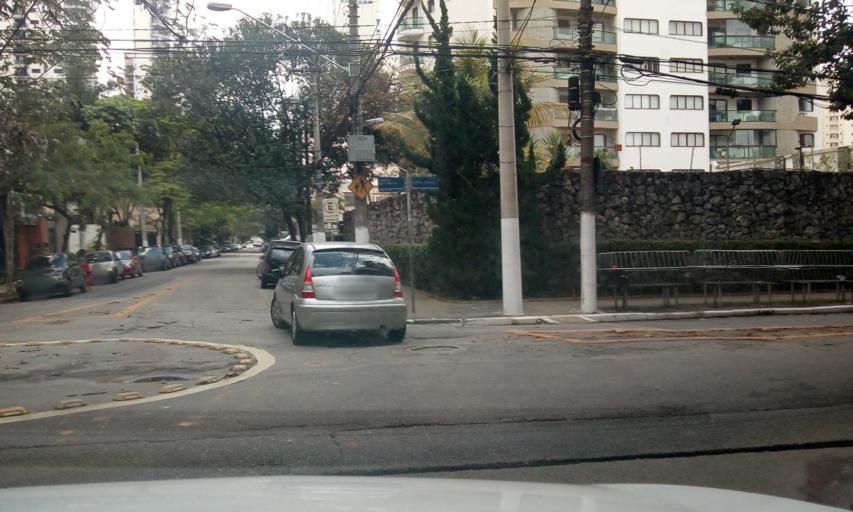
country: BR
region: Sao Paulo
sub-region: Sao Paulo
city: Sao Paulo
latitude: -23.6051
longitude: -46.6560
